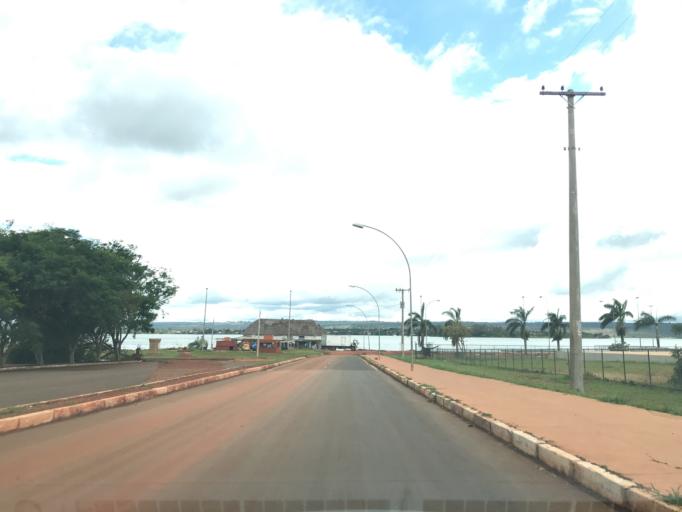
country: BR
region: Federal District
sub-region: Brasilia
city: Brasilia
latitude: -15.7873
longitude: -47.8376
